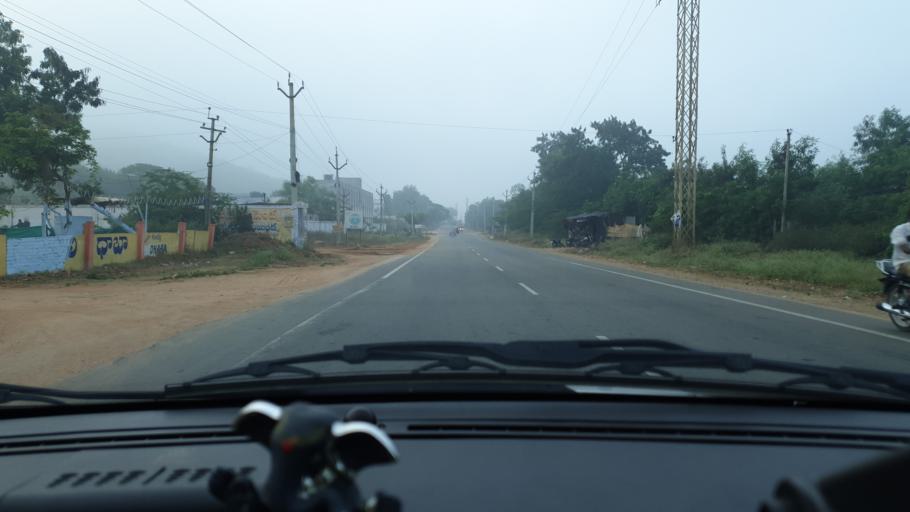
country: IN
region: Telangana
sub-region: Mahbubnagar
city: Farrukhnagar
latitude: 16.8735
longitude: 78.5293
